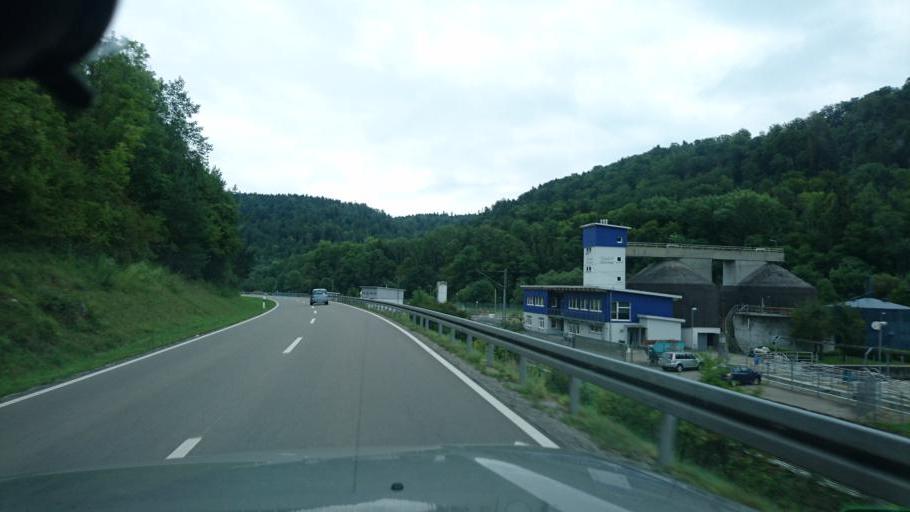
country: DE
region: Baden-Wuerttemberg
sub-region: Freiburg Region
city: Oberndorf
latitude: 48.3205
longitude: 8.5841
